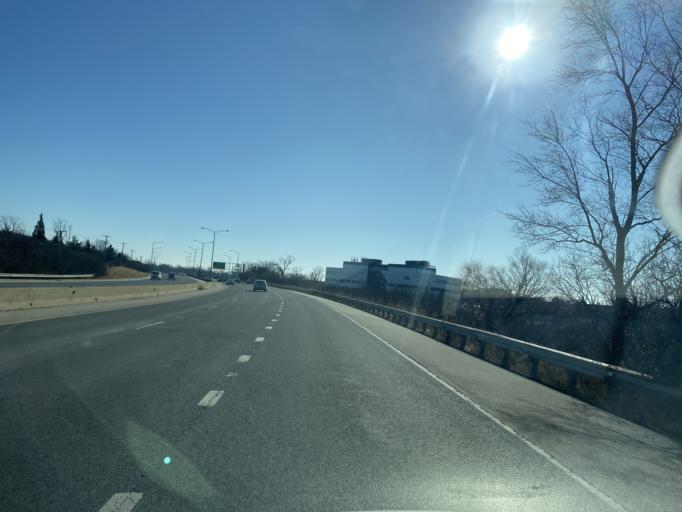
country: US
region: Illinois
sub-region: DuPage County
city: Clarendon Hills
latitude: 41.8171
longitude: -87.9525
